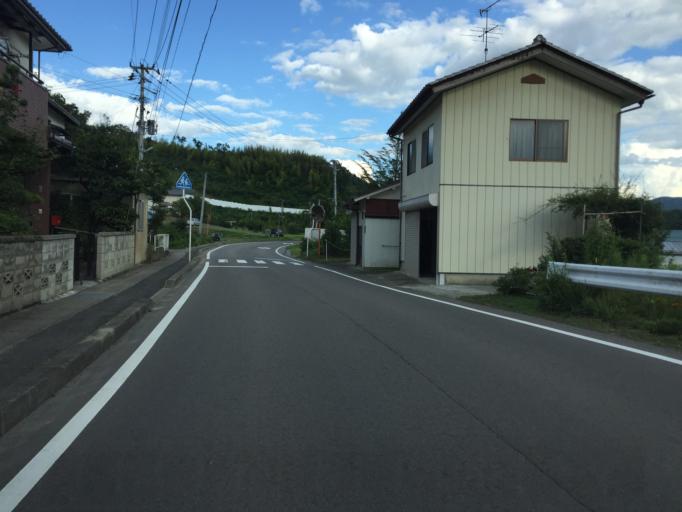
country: JP
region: Fukushima
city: Fukushima-shi
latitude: 37.6770
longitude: 140.5816
